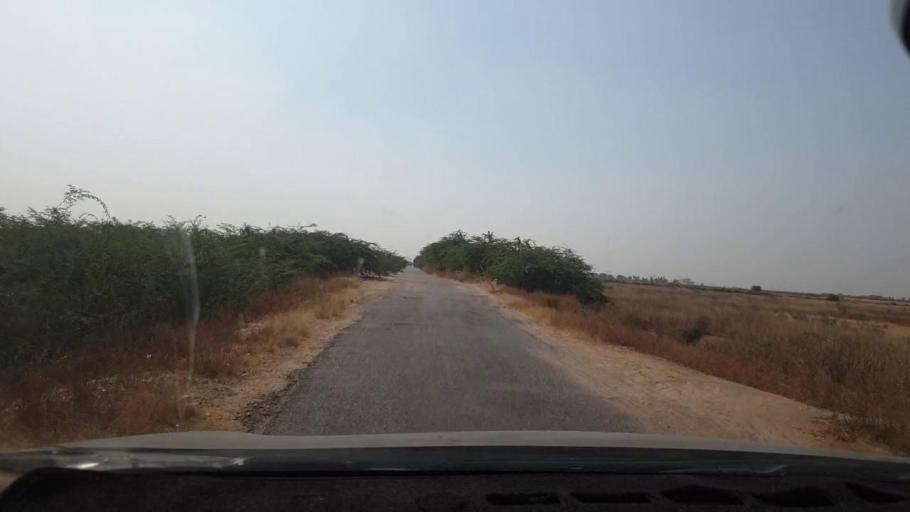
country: PK
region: Sindh
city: Malir Cantonment
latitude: 25.1201
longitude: 67.2162
